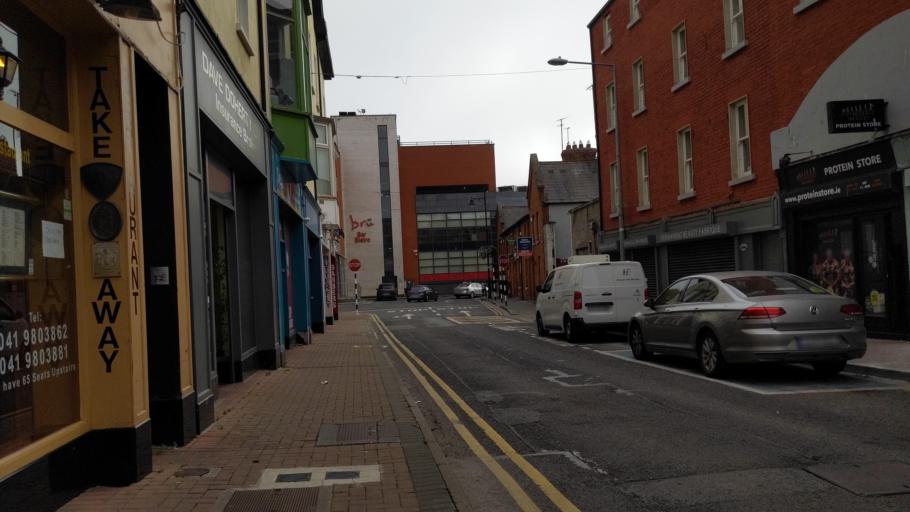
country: IE
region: Leinster
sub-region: Lu
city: Drogheda
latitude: 53.7143
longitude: -6.3530
